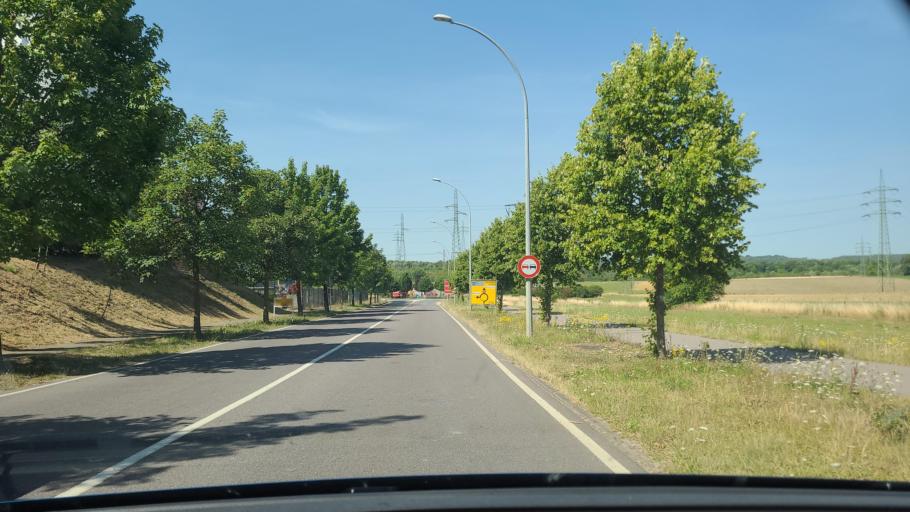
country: LU
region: Luxembourg
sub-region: Canton d'Esch-sur-Alzette
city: Sanem
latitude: 49.5387
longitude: 5.9369
